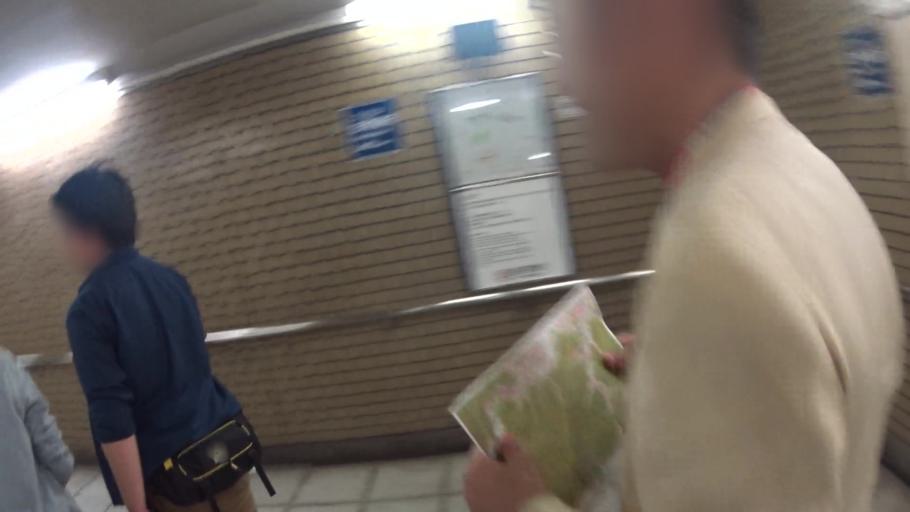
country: JP
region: Tokyo
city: Tokyo
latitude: 35.7362
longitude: 139.6908
